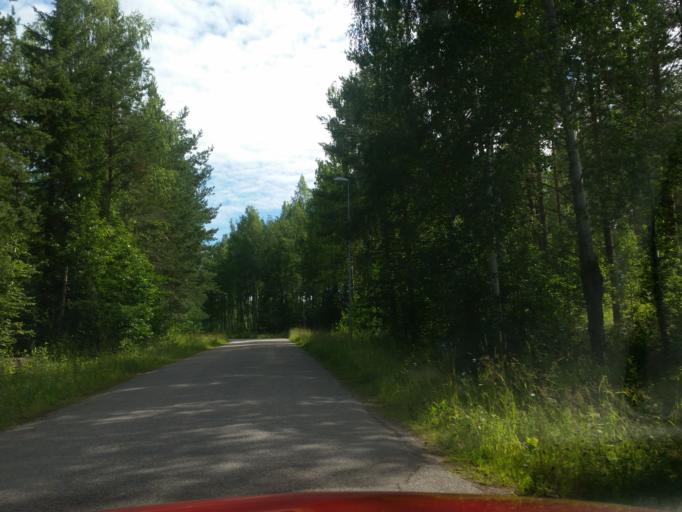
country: SE
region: Dalarna
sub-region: Leksand Municipality
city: Smedby
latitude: 60.6622
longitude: 15.1112
